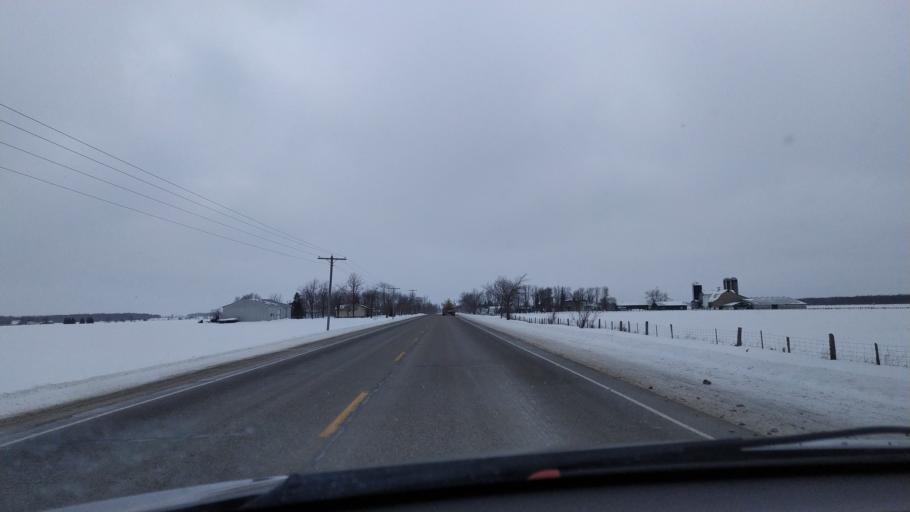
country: CA
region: Ontario
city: North Perth
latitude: 43.5827
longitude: -80.8612
